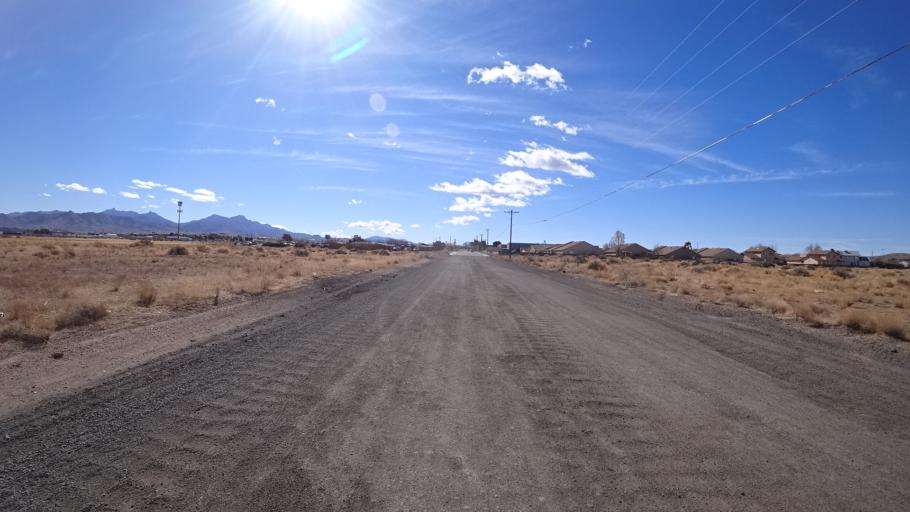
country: US
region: Arizona
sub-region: Mohave County
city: New Kingman-Butler
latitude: 35.2224
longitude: -114.0204
